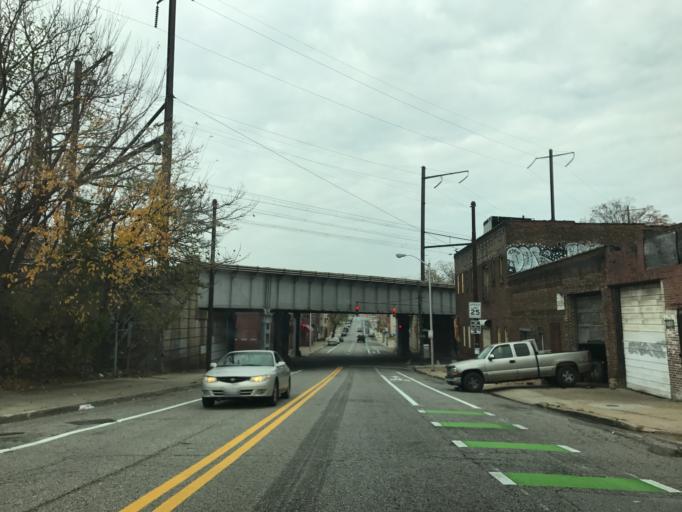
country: US
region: Maryland
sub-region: City of Baltimore
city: Baltimore
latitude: 39.3055
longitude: -76.5905
